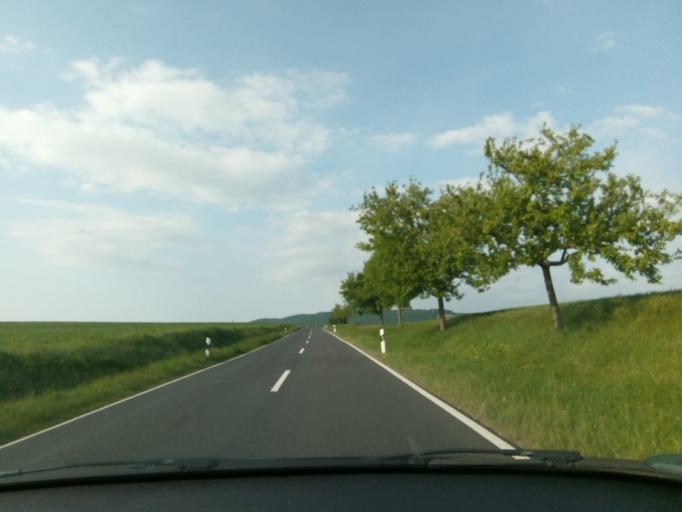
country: DE
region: Bavaria
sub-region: Regierungsbezirk Unterfranken
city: Oberschwarzach
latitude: 49.8528
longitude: 10.4074
